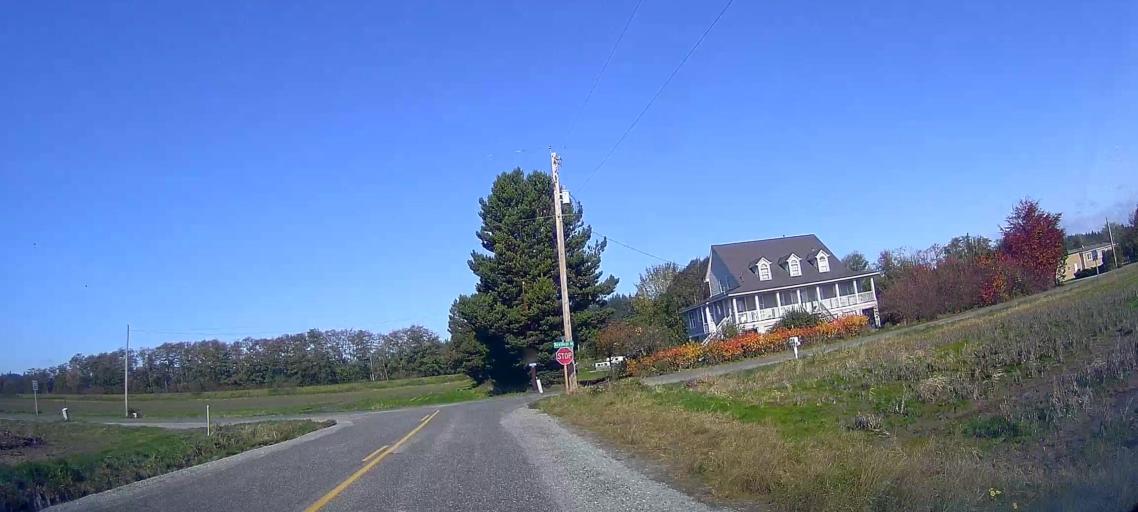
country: US
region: Washington
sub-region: Skagit County
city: Mount Vernon
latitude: 48.3551
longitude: -122.4389
